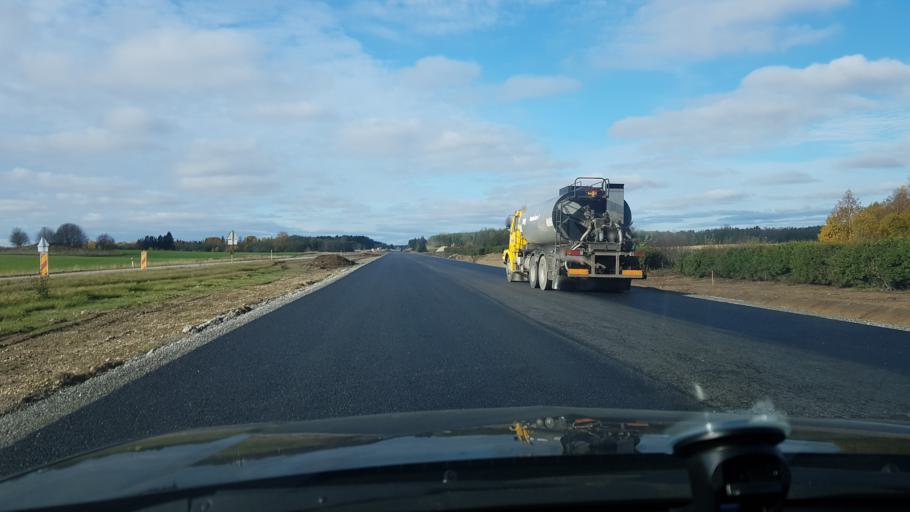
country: EE
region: Laeaene-Virumaa
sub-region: Kadrina vald
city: Kadrina
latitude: 59.4425
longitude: 26.1076
